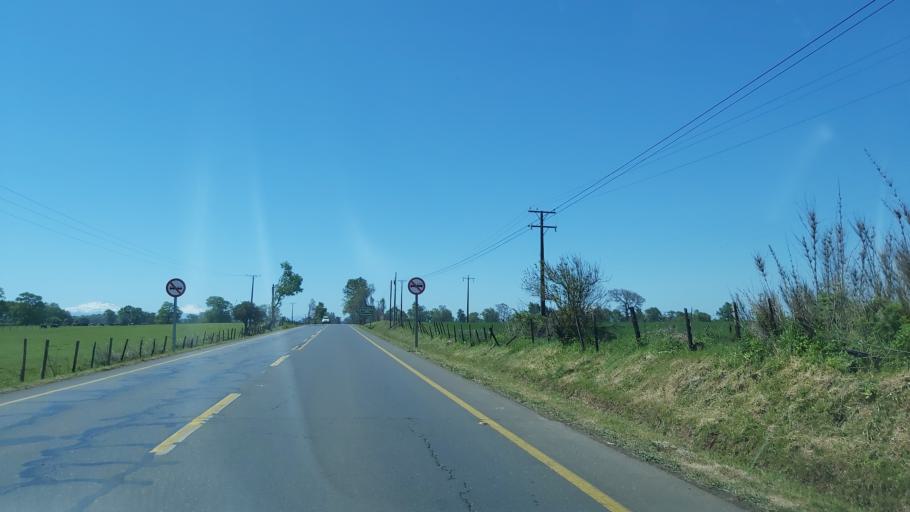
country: CL
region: Araucania
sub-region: Provincia de Malleco
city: Victoria
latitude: -38.2473
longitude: -72.3097
